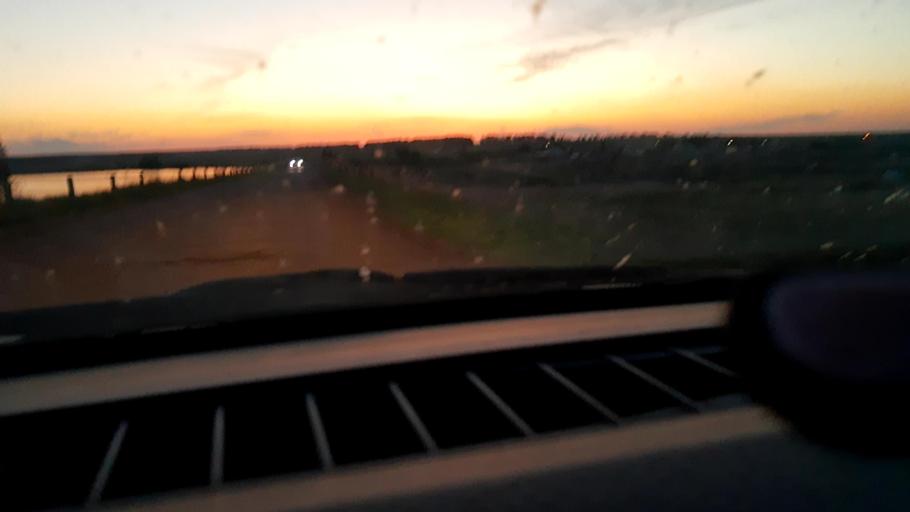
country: RU
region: Bashkortostan
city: Asanovo
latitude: 54.8502
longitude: 55.5923
